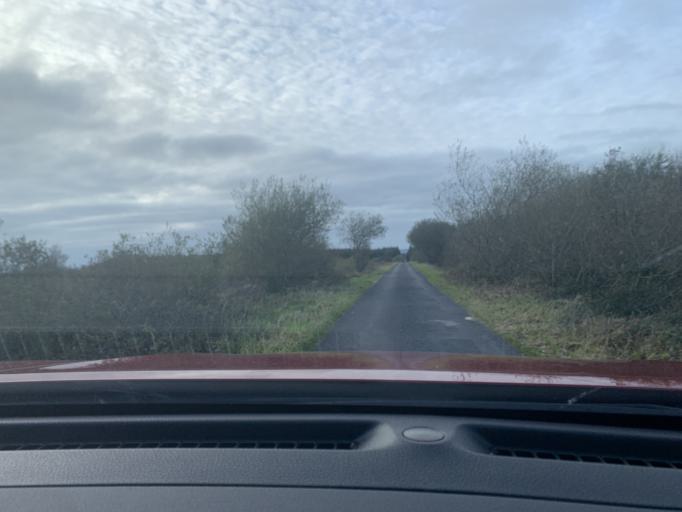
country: IE
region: Connaught
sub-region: Roscommon
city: Ballaghaderreen
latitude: 53.9654
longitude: -8.6112
